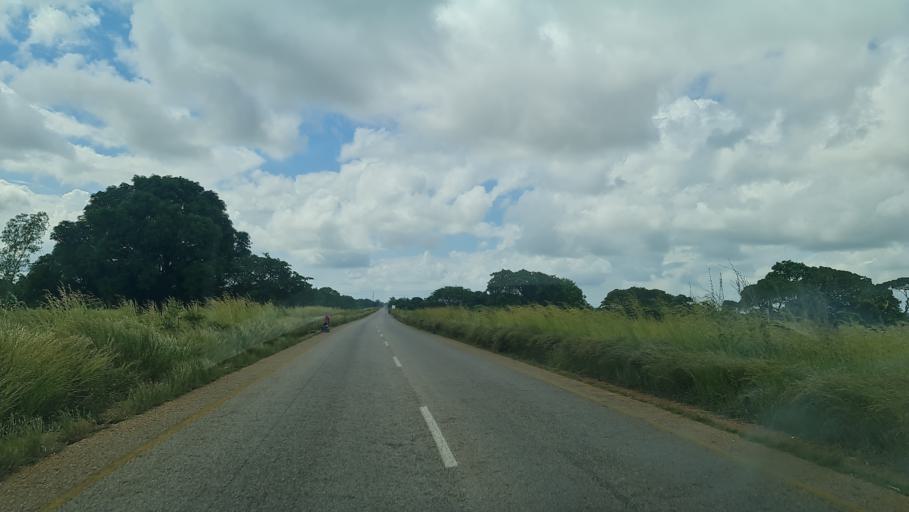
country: MZ
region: Nampula
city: Nampula
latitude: -14.9318
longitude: 39.9593
